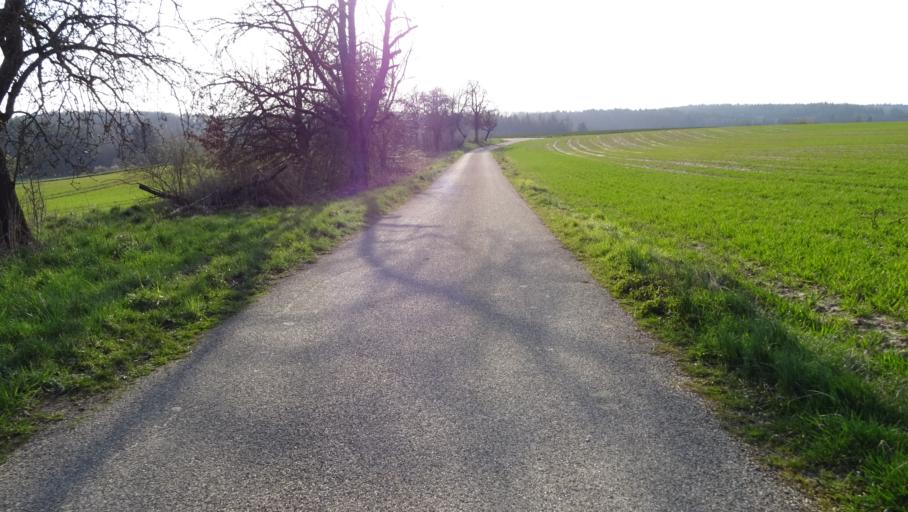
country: DE
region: Baden-Wuerttemberg
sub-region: Regierungsbezirk Stuttgart
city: Roigheim
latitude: 49.3818
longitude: 9.3547
